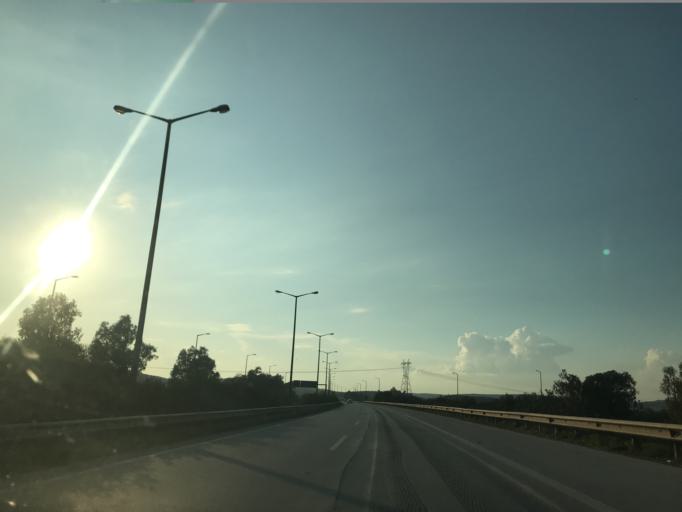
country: TR
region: Osmaniye
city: Toprakkale
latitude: 36.9752
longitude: 36.0179
